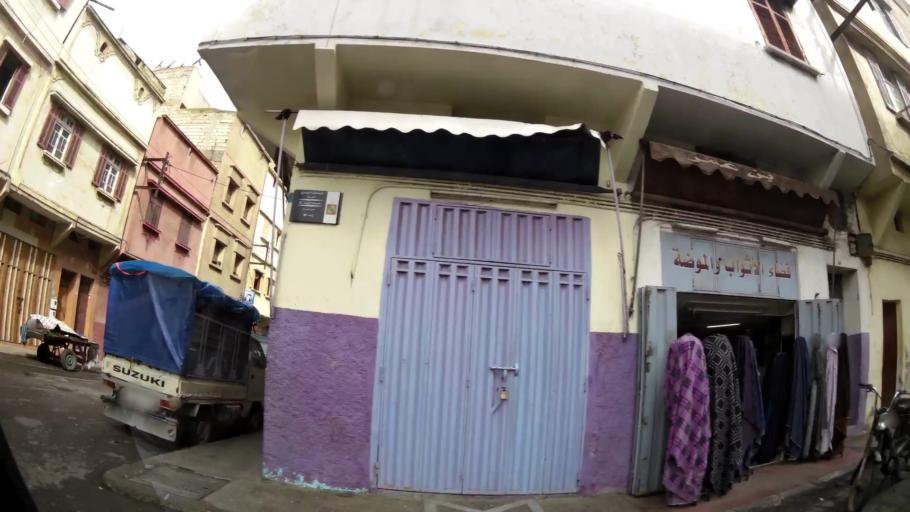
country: MA
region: Grand Casablanca
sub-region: Casablanca
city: Casablanca
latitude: 33.5694
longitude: -7.5877
